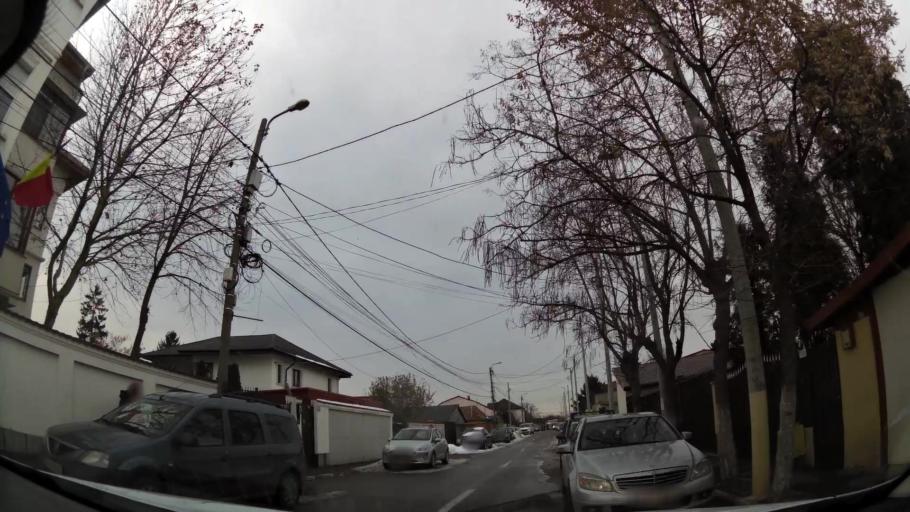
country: RO
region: Ilfov
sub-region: Voluntari City
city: Voluntari
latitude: 44.4848
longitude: 26.1876
